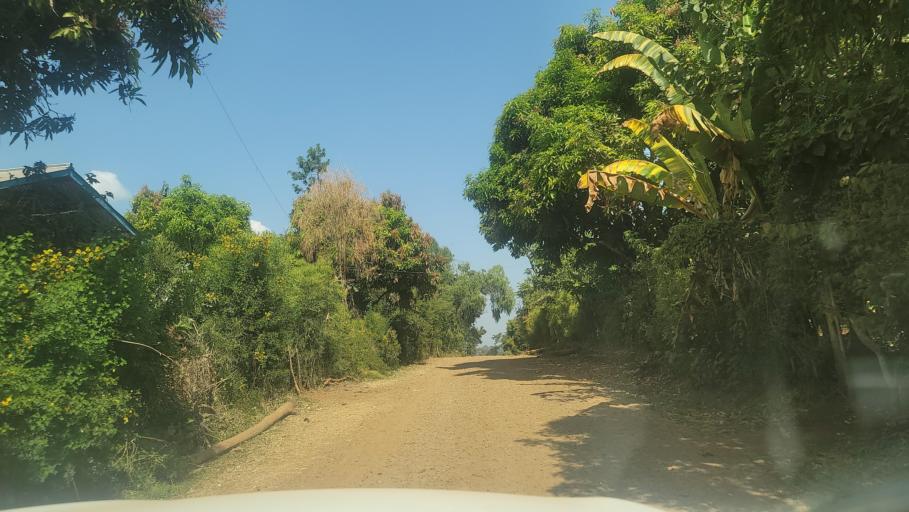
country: ET
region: Oromiya
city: Agaro
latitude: 7.8500
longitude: 36.5390
